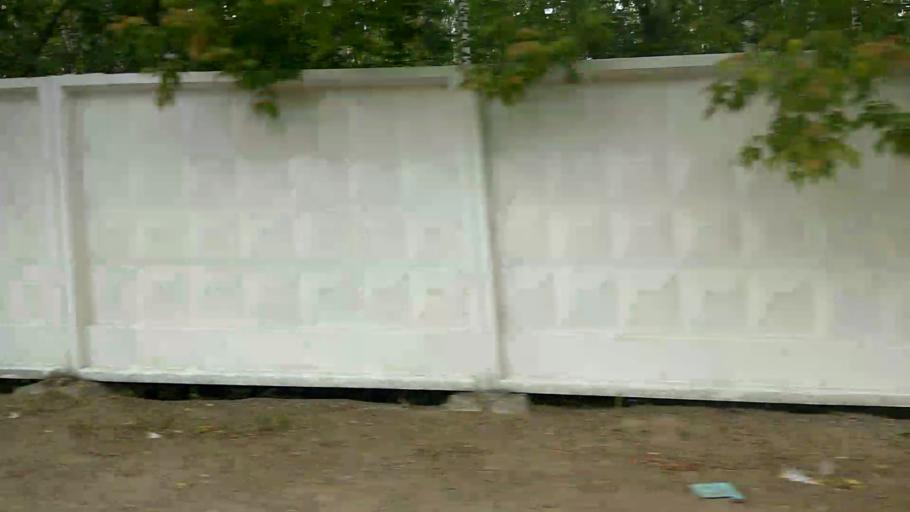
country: RU
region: Moskovskaya
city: Ramenskoye
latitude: 55.5678
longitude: 38.2609
